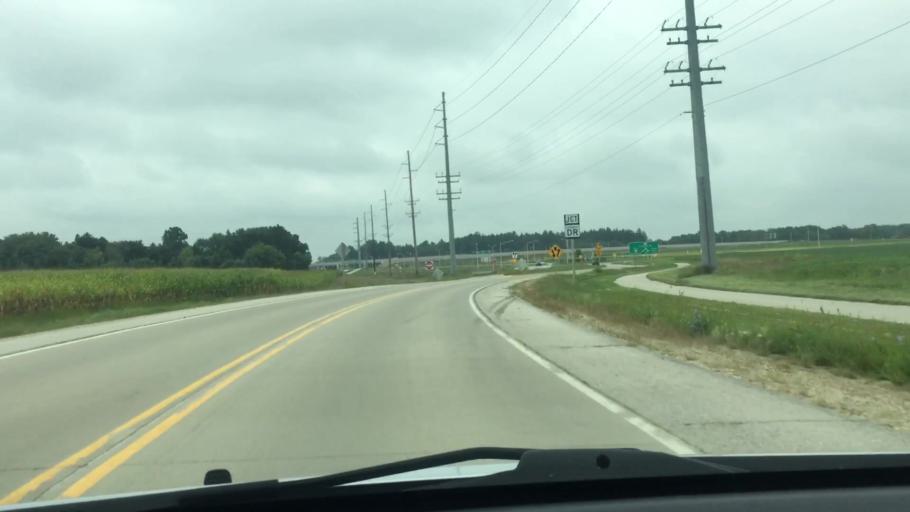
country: US
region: Wisconsin
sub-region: Waukesha County
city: Delafield
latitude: 43.0673
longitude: -88.4422
